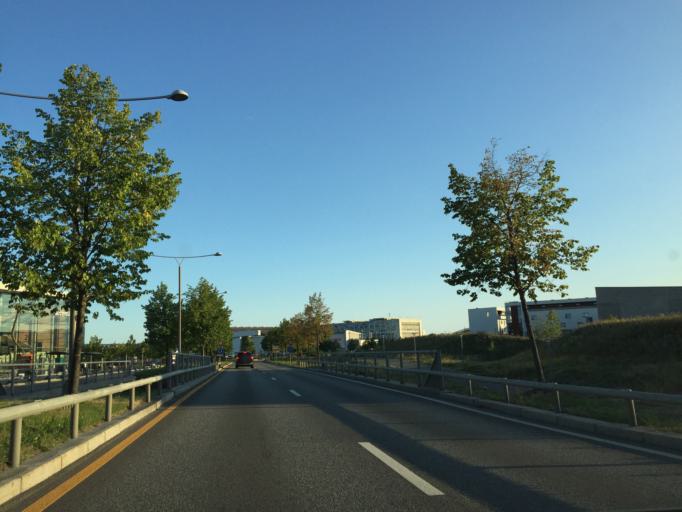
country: NO
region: Akershus
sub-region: Baerum
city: Lysaker
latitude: 59.8967
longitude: 10.6259
